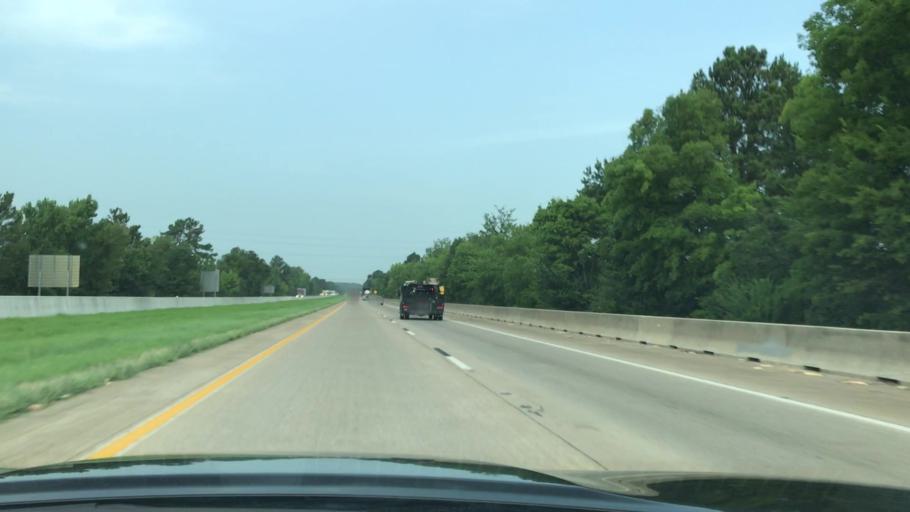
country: US
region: Texas
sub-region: Gregg County
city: Longview
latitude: 32.4407
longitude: -94.7360
